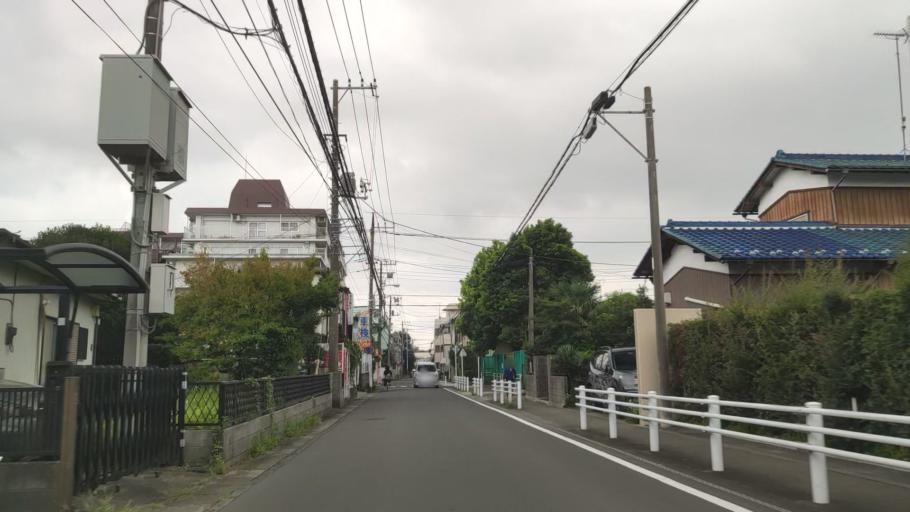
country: JP
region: Kanagawa
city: Minami-rinkan
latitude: 35.4912
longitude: 139.4608
